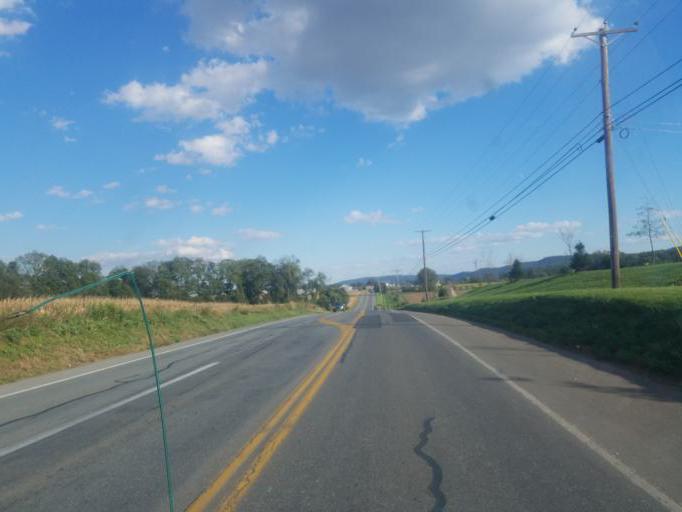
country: US
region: Pennsylvania
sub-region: Lancaster County
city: Bainbridge
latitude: 40.0741
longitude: -76.6403
